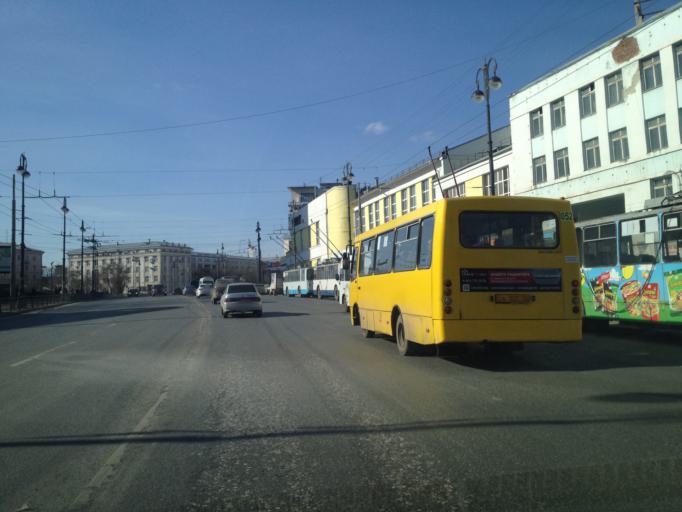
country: RU
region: Sverdlovsk
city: Yekaterinburg
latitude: 56.8484
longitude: 60.6085
